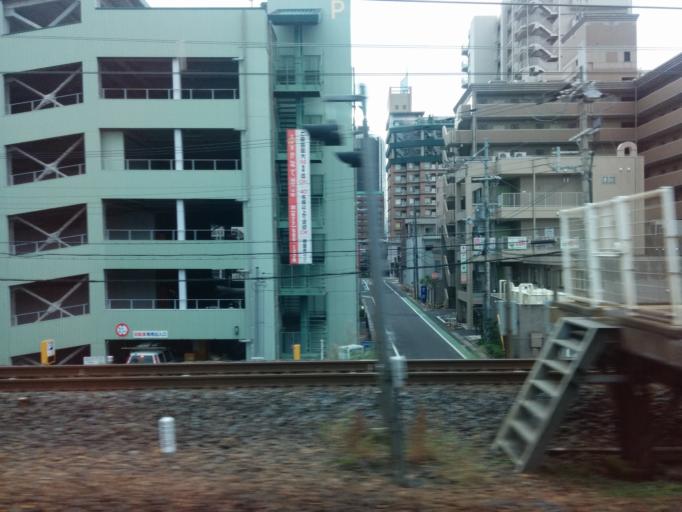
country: JP
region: Shiga Prefecture
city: Kusatsu
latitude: 35.0045
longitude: 135.9478
